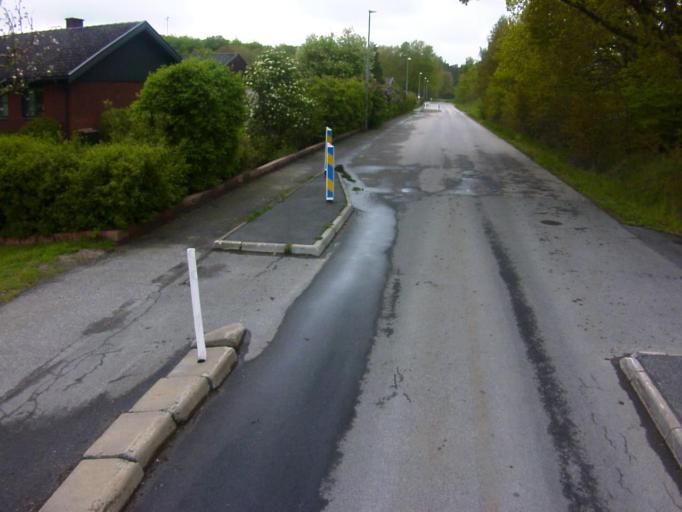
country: SE
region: Blekinge
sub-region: Solvesborgs Kommun
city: Soelvesborg
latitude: 56.0632
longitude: 14.5827
